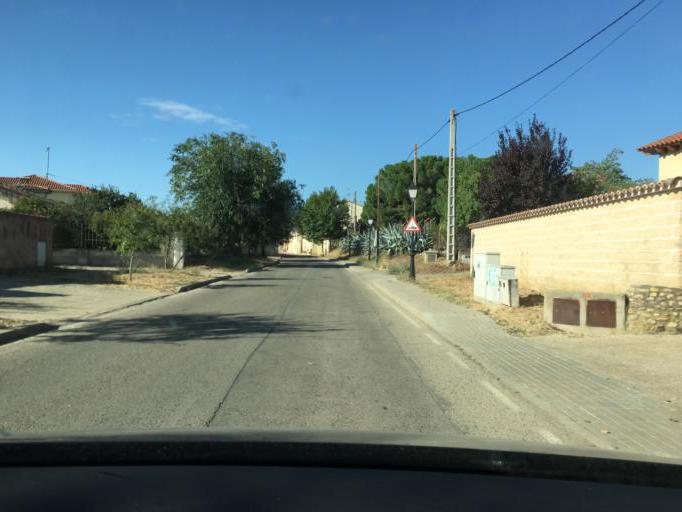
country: ES
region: Madrid
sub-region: Provincia de Madrid
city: Torremocha de Jarama
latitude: 40.8367
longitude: -3.4938
